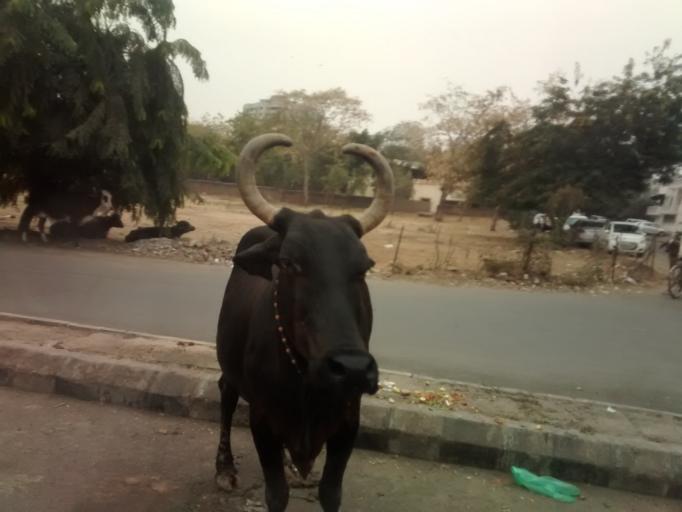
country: IN
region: Gujarat
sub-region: Ahmadabad
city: Sarkhej
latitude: 23.0332
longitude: 72.5219
